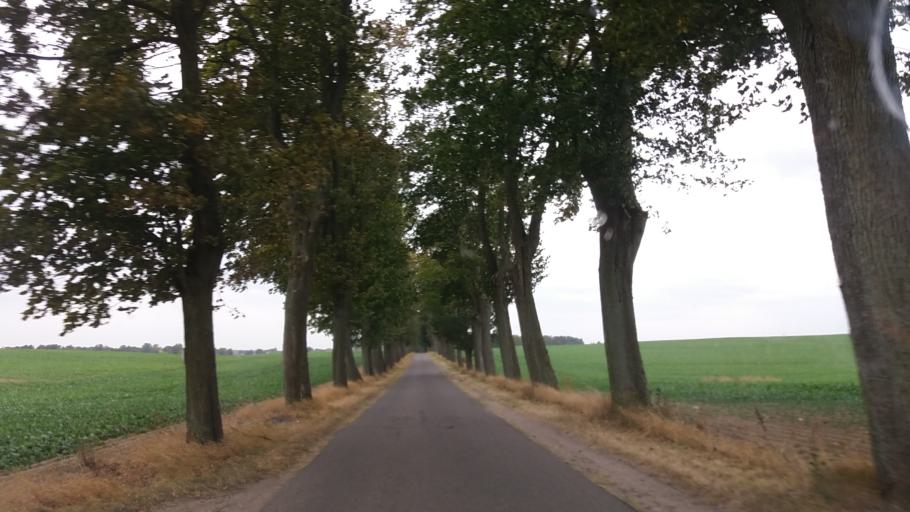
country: PL
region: West Pomeranian Voivodeship
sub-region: Powiat choszczenski
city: Bierzwnik
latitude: 52.9810
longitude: 15.5837
